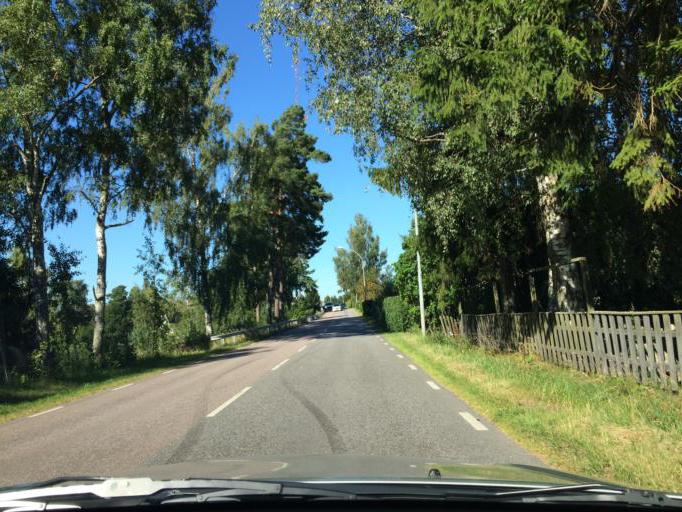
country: SE
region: Soedermanland
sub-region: Eskilstuna Kommun
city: Skogstorp
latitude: 59.3361
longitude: 16.4318
